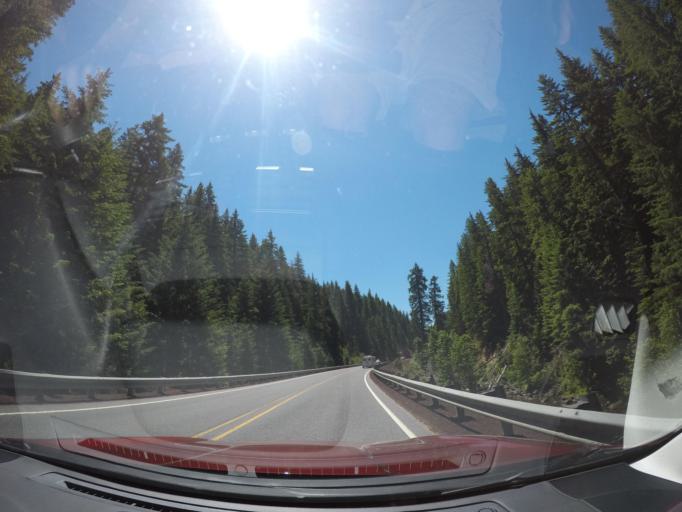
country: US
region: Oregon
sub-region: Deschutes County
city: Sisters
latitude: 44.5530
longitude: -121.9939
